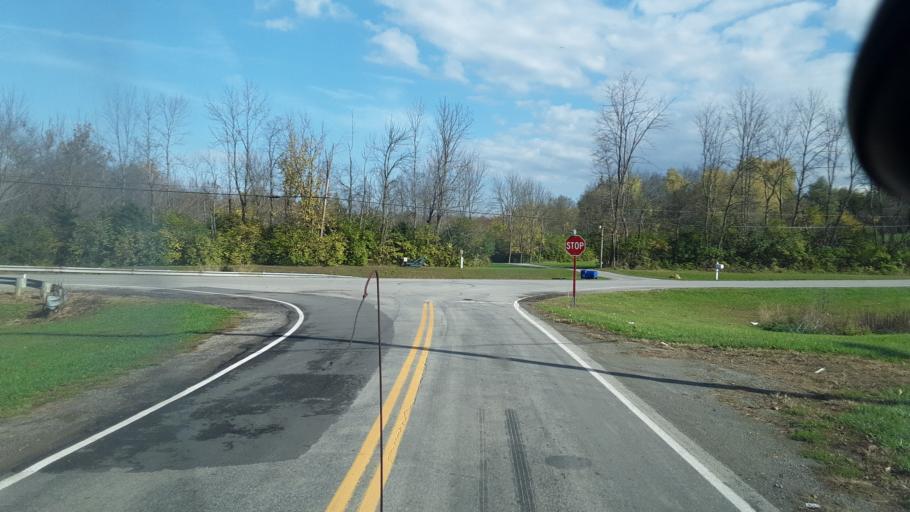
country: US
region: Ohio
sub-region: Highland County
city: Leesburg
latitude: 39.3467
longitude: -83.5839
